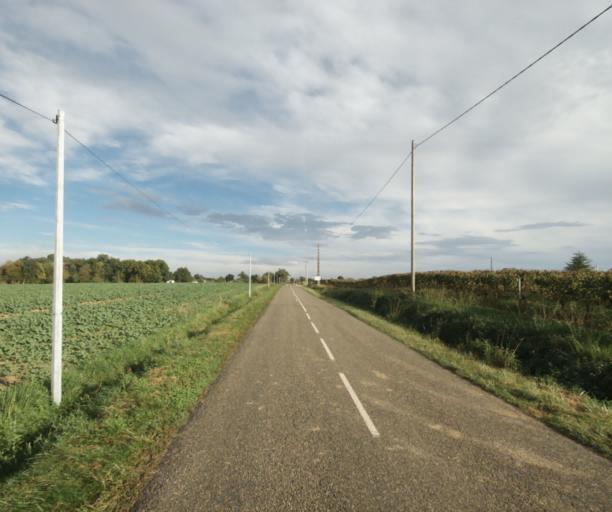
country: FR
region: Midi-Pyrenees
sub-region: Departement du Gers
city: Le Houga
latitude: 43.8588
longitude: -0.1472
